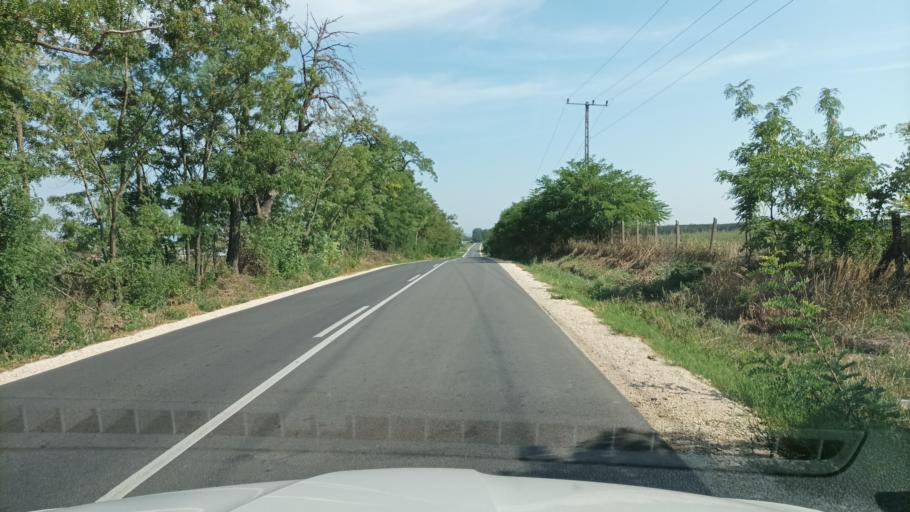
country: HU
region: Pest
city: Galgaheviz
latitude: 47.5906
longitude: 19.5722
